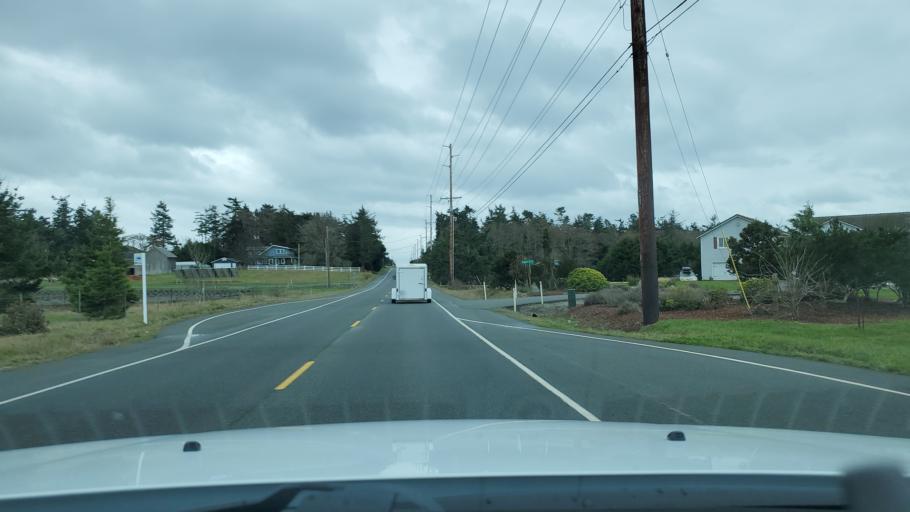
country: US
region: Washington
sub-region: Island County
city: Coupeville
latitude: 48.2487
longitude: -122.7517
